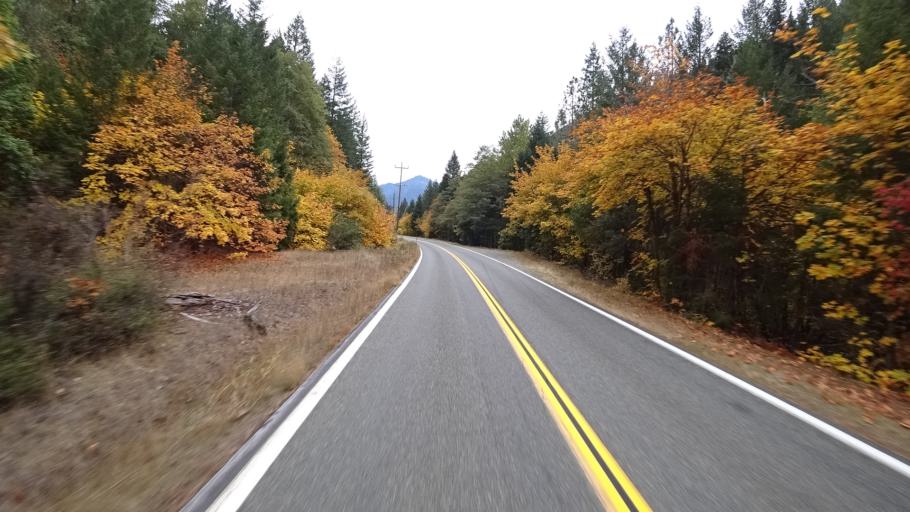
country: US
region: California
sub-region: Siskiyou County
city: Happy Camp
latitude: 41.9043
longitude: -123.4407
